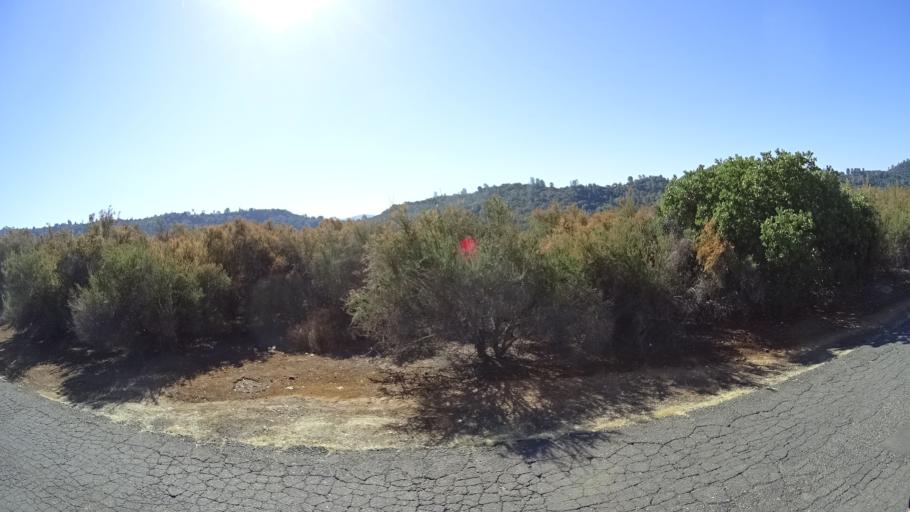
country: US
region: California
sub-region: Calaveras County
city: Murphys
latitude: 38.0733
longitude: -120.4648
